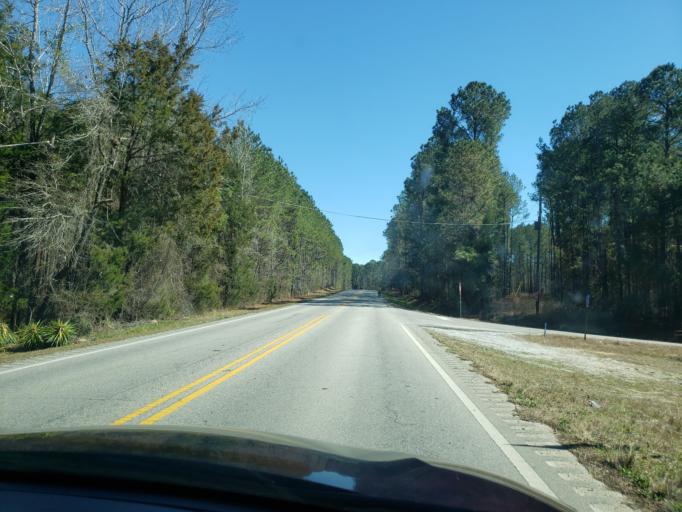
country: US
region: Alabama
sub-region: Lee County
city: Auburn
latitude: 32.5962
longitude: -85.6276
